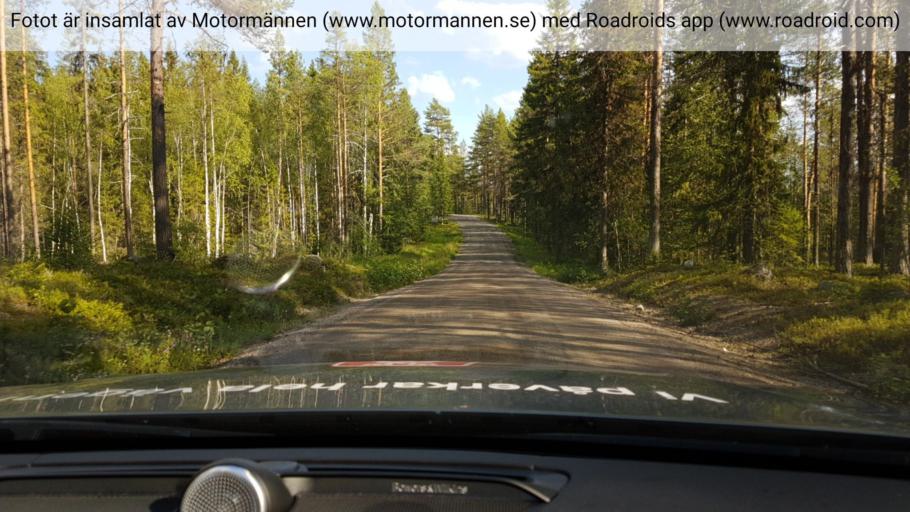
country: SE
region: Vaesterbotten
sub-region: Dorotea Kommun
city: Dorotea
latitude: 63.9750
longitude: 16.0517
